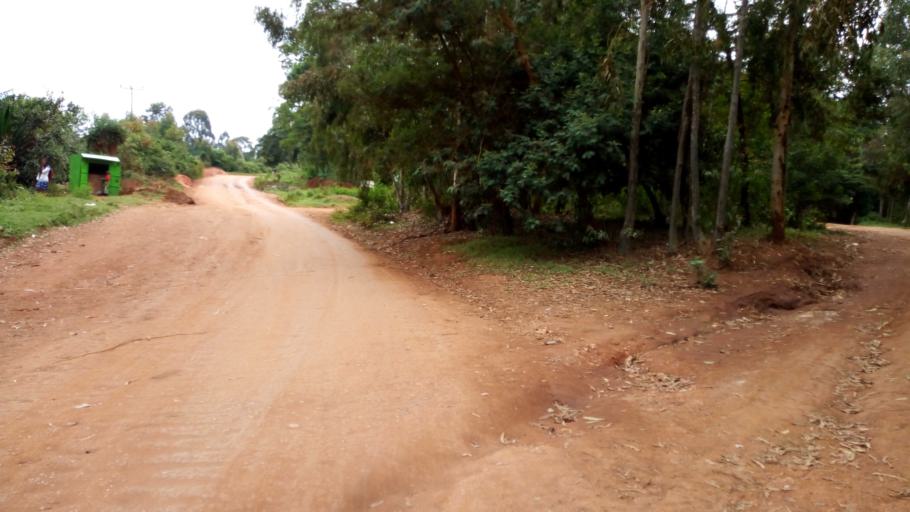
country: KE
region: Makueni
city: Wote
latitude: -1.6605
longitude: 37.4547
